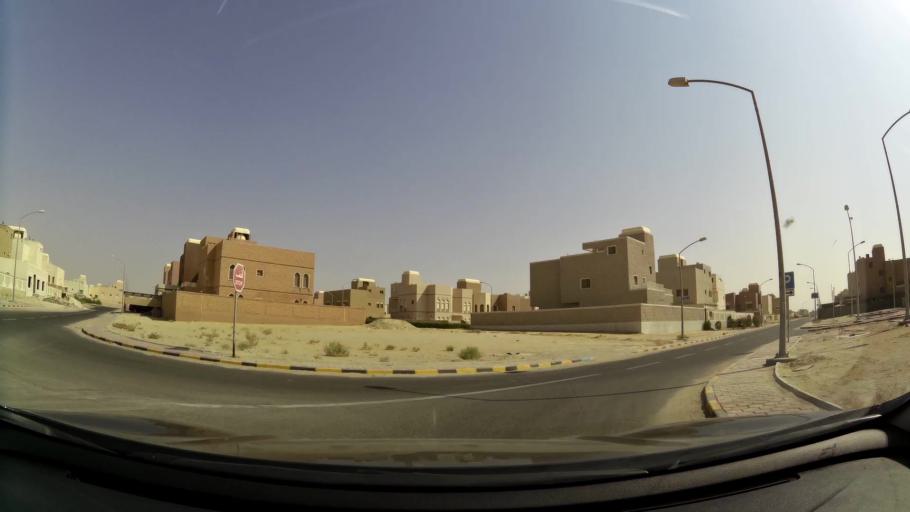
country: KW
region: Al Ahmadi
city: Al Wafrah
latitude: 28.8064
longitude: 48.0490
